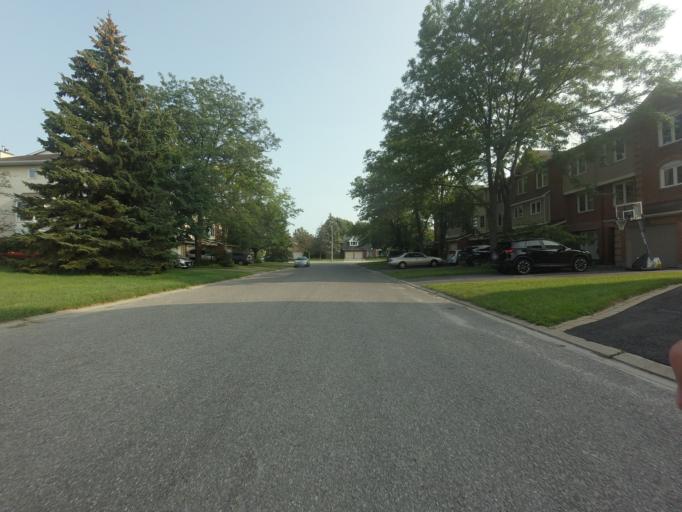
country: CA
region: Ontario
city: Bells Corners
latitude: 45.3386
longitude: -75.7636
